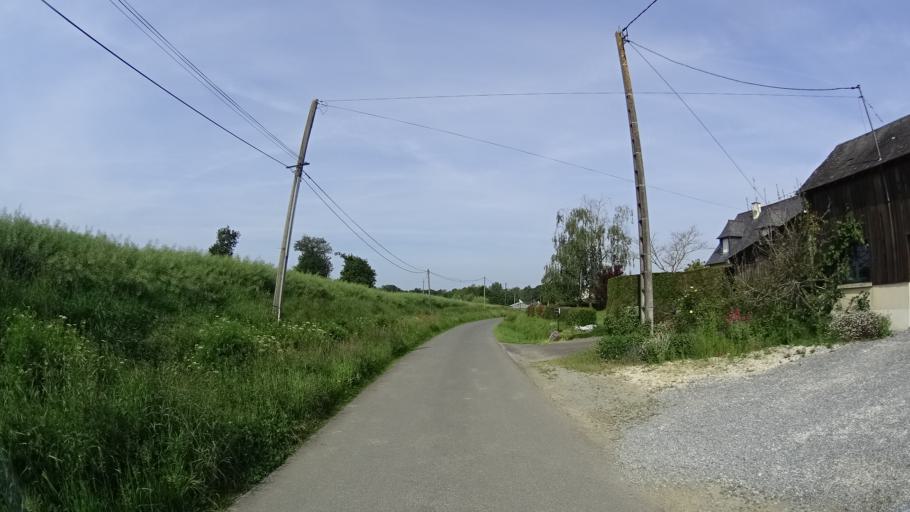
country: FR
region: Brittany
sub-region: Departement d'Ille-et-Vilaine
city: Nouvoitou
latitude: 48.0217
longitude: -1.5441
